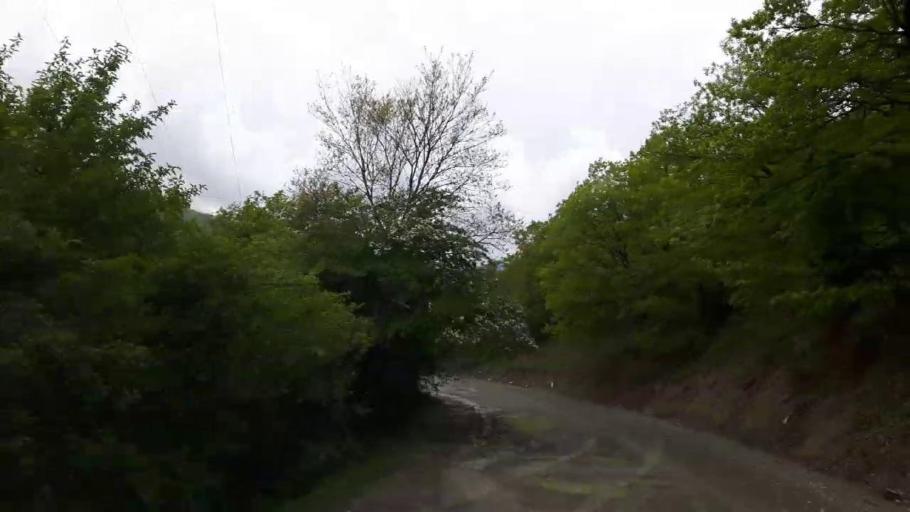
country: GE
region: Shida Kartli
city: Gori
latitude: 41.8742
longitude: 43.9880
